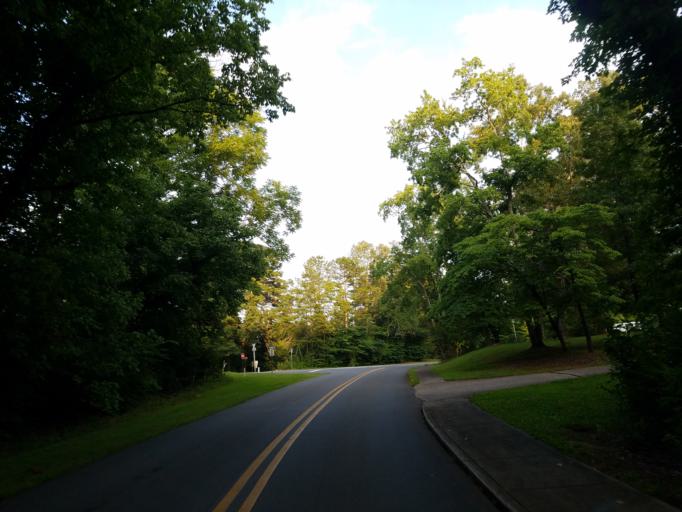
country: US
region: Georgia
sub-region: Pickens County
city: Nelson
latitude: 34.4222
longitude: -84.3918
